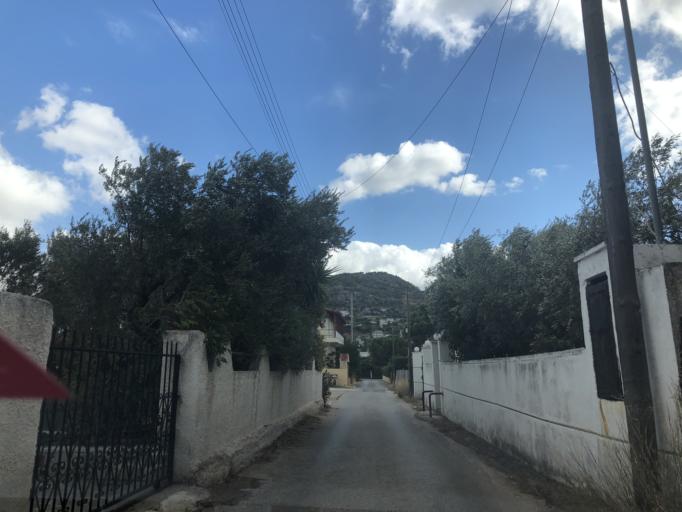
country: GR
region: Attica
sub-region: Nomarchia Anatolikis Attikis
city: Agia Marina
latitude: 37.8219
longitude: 23.8426
